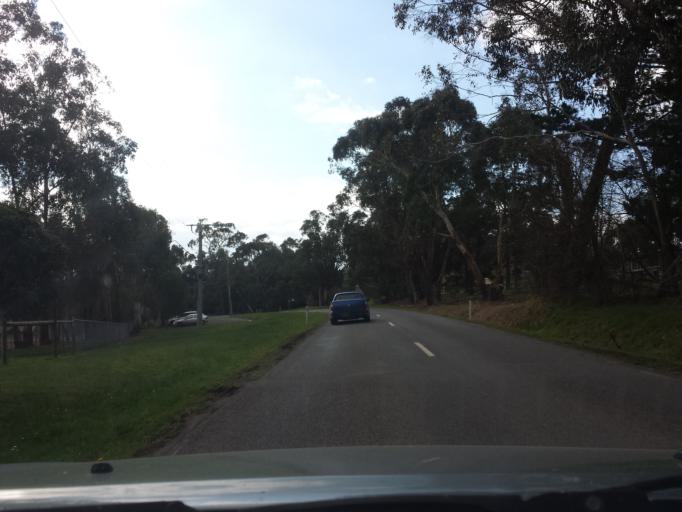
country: AU
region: Victoria
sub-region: Yarra Ranges
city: Woori Yallock
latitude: -37.7812
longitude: 145.4637
